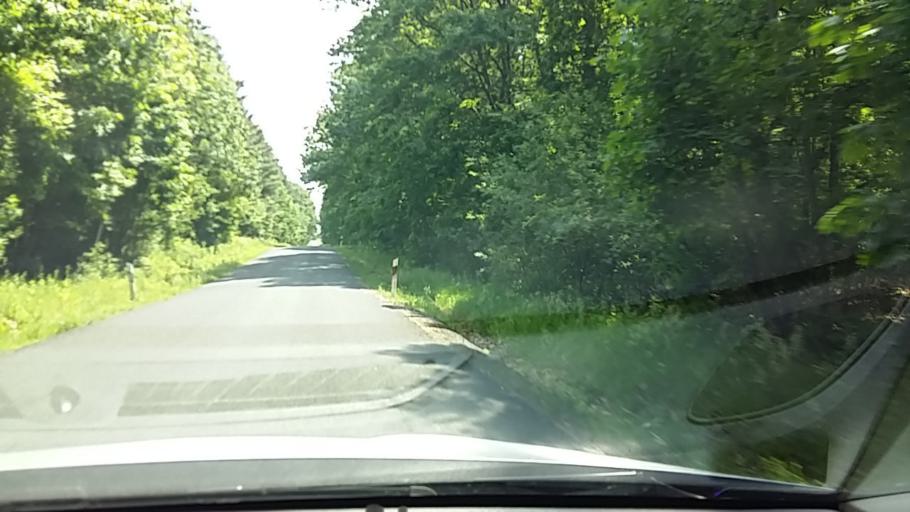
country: HU
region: Vas
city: Kormend
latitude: 46.9662
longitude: 16.5808
